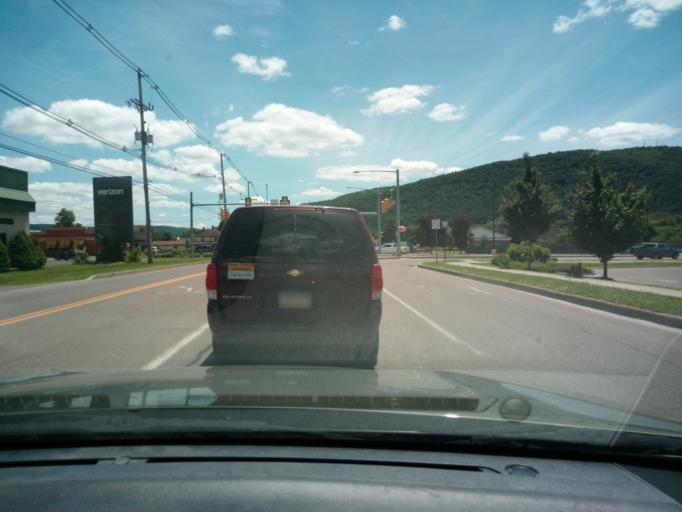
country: US
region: Pennsylvania
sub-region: Bradford County
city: South Waverly
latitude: 41.9765
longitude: -76.5414
